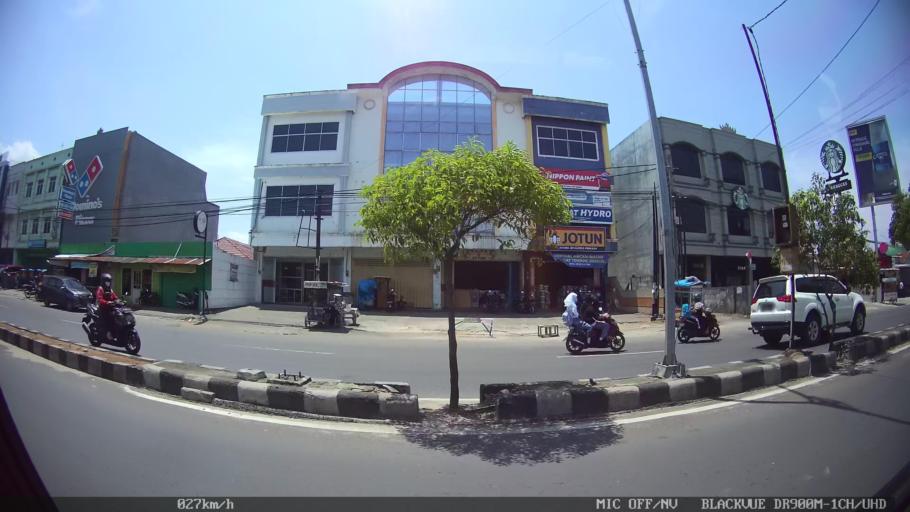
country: ID
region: Lampung
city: Kedaton
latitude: -5.4045
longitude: 105.2792
